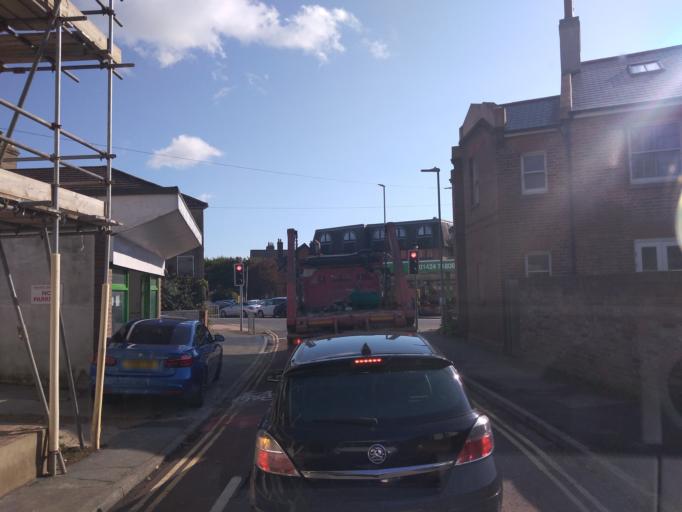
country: GB
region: England
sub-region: East Sussex
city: Saint Leonards-on-Sea
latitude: 50.8635
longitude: 0.5504
